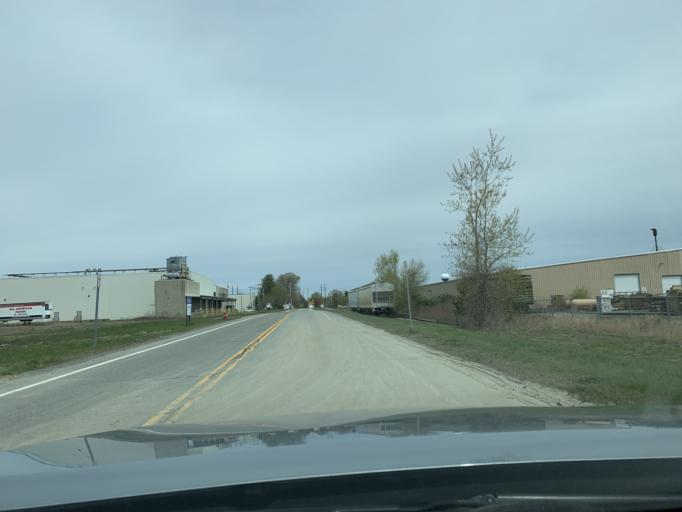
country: US
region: Rhode Island
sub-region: Washington County
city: North Kingstown
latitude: 41.6014
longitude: -71.4698
